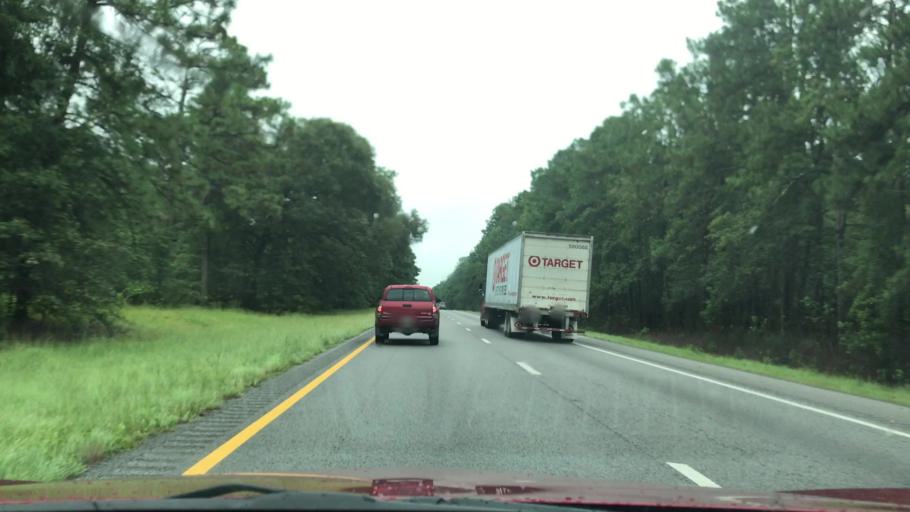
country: US
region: South Carolina
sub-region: Dorchester County
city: Ridgeville
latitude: 33.1622
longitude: -80.3561
